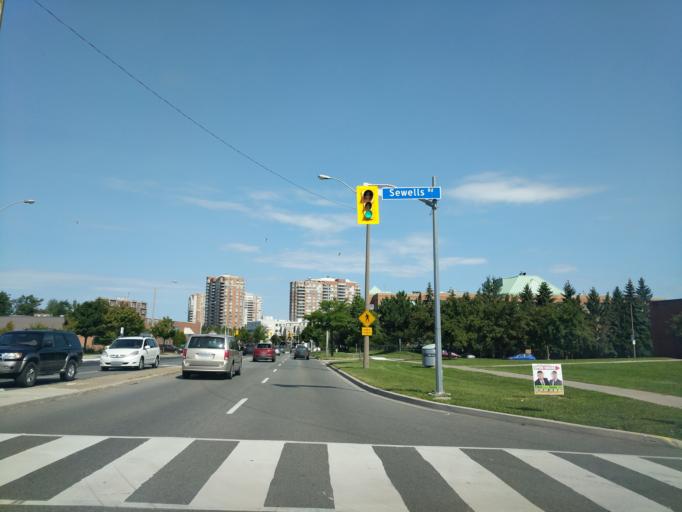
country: CA
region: Ontario
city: Scarborough
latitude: 43.8067
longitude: -79.2186
